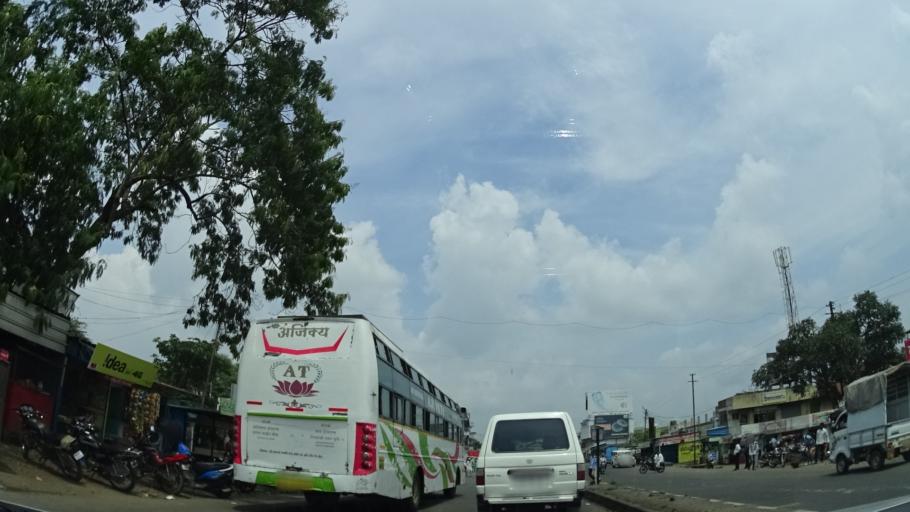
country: IN
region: Maharashtra
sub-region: Pune Division
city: Sirur
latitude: 18.9575
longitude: 74.5371
